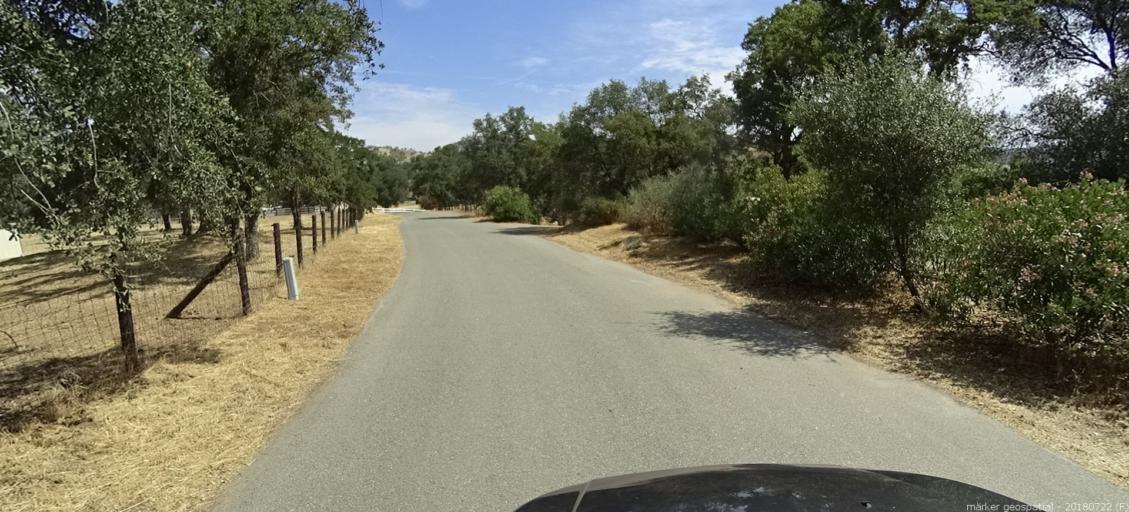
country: US
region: California
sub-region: Madera County
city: Coarsegold
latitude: 37.2574
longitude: -119.7133
